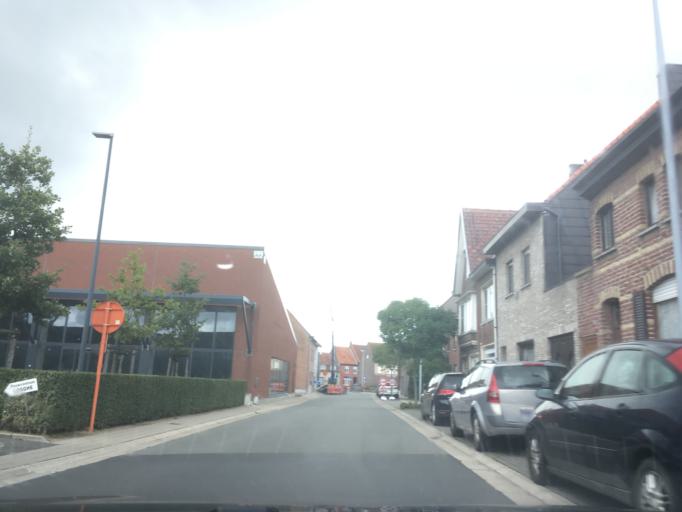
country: BE
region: Flanders
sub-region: Provincie West-Vlaanderen
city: Kortemark
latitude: 51.0242
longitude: 3.0412
